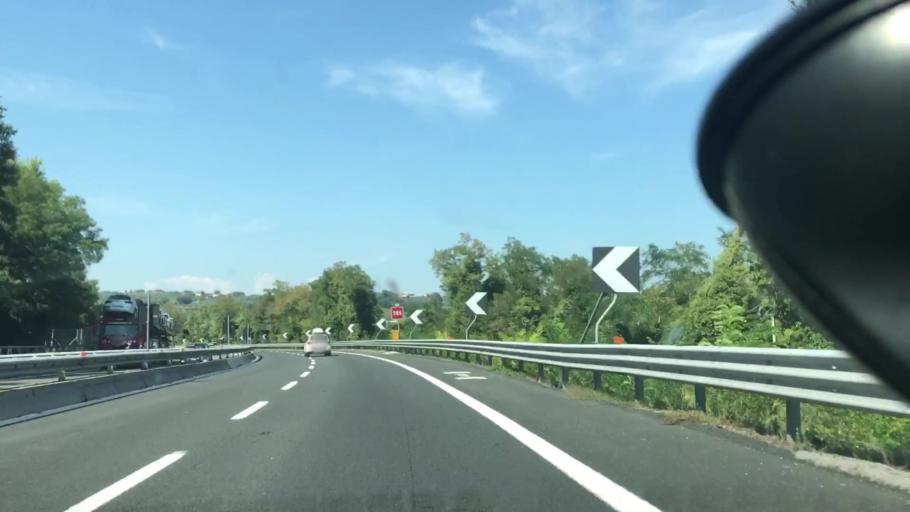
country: IT
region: Abruzzo
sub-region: Provincia di Chieti
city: Torino di Sangro
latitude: 42.2046
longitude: 14.5515
